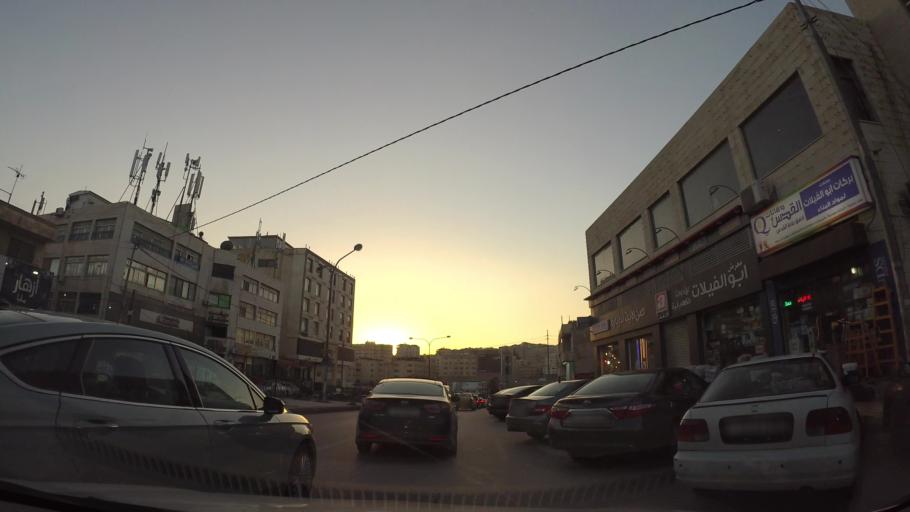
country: JO
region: Amman
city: Al Jubayhah
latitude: 31.9933
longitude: 35.8630
